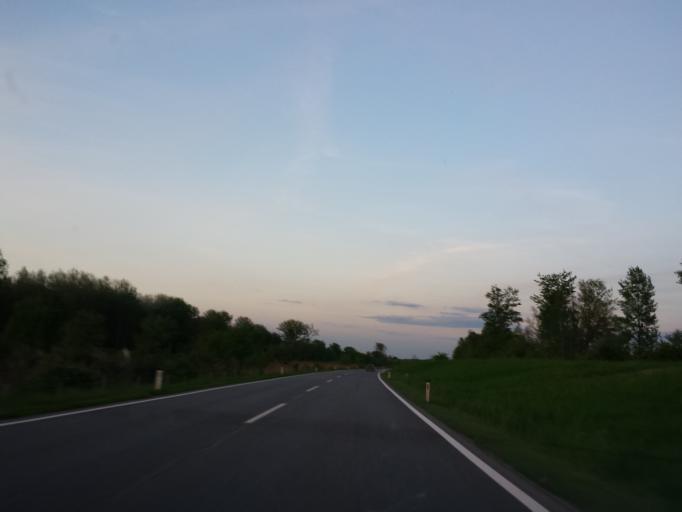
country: AT
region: Lower Austria
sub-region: Politischer Bezirk Tulln
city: Tulln
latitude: 48.3371
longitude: 16.0366
